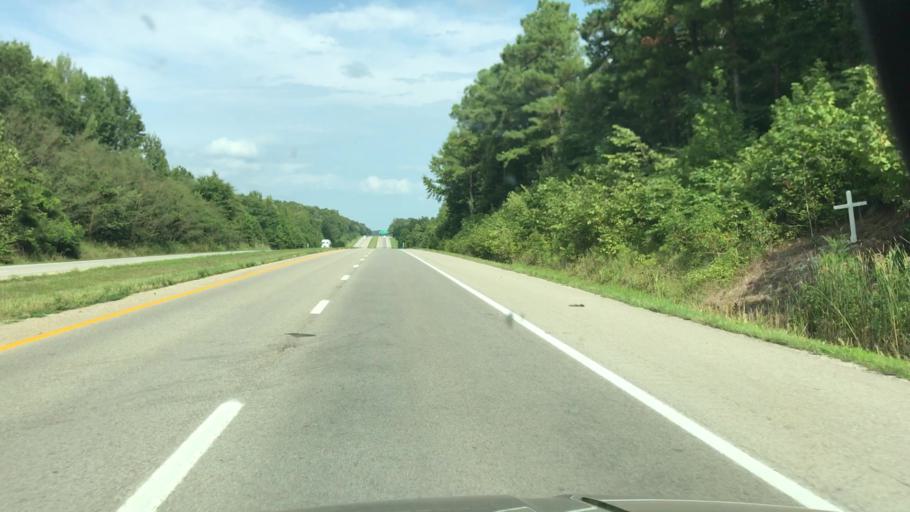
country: US
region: Kentucky
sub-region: Hopkins County
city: Nortonville
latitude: 37.2058
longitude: -87.5059
